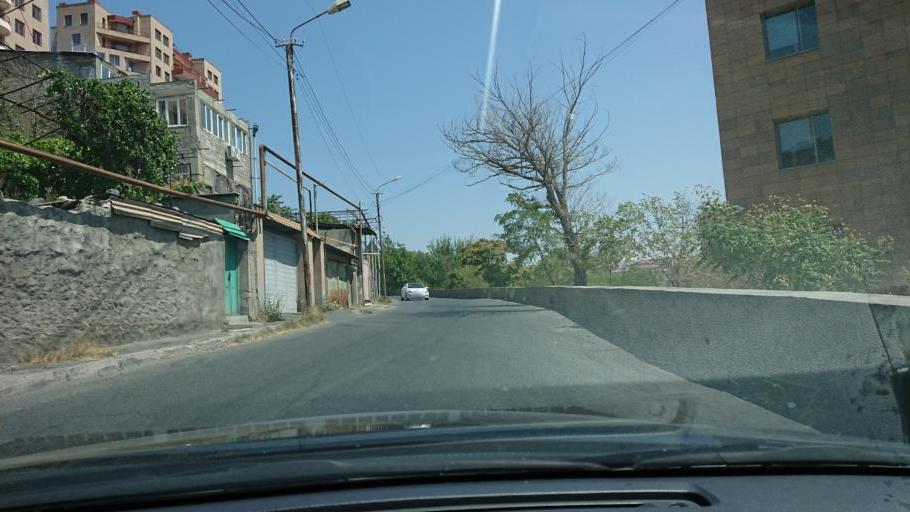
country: AM
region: Yerevan
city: Yerevan
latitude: 40.1936
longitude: 44.5028
